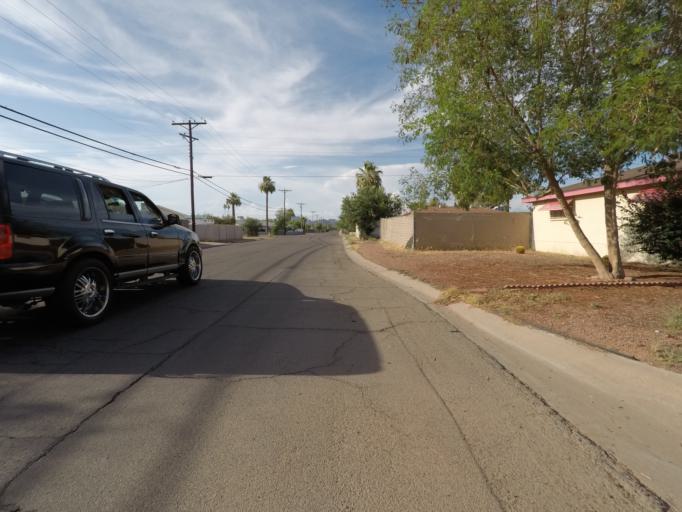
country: US
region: Arizona
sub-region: Maricopa County
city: Phoenix
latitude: 33.4688
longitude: -112.0085
